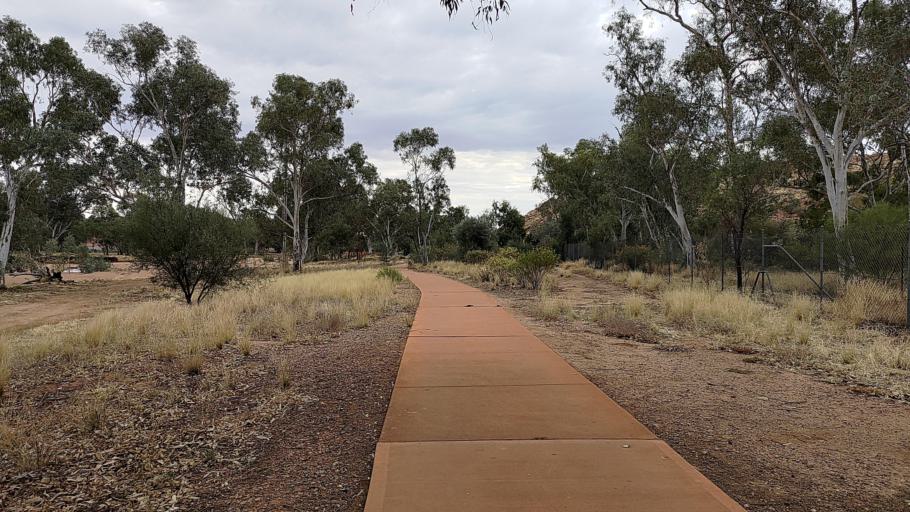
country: AU
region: Northern Territory
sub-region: Alice Springs
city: Alice Springs
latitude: -23.7068
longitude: 133.8824
